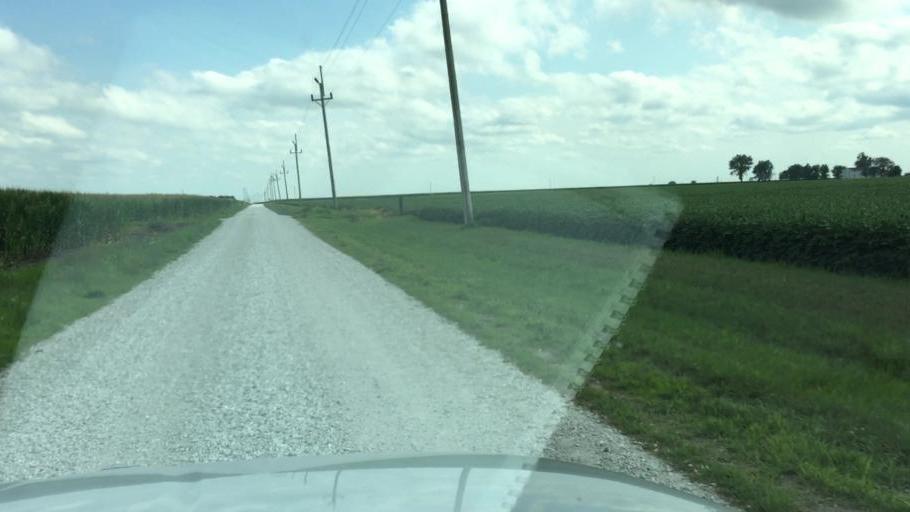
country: US
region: Illinois
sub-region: Hancock County
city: Carthage
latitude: 40.4107
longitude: -91.1786
